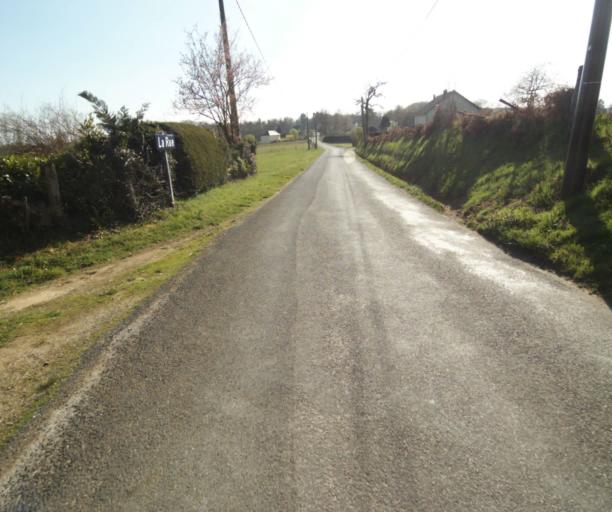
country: FR
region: Limousin
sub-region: Departement de la Correze
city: Saint-Mexant
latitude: 45.3212
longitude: 1.6246
